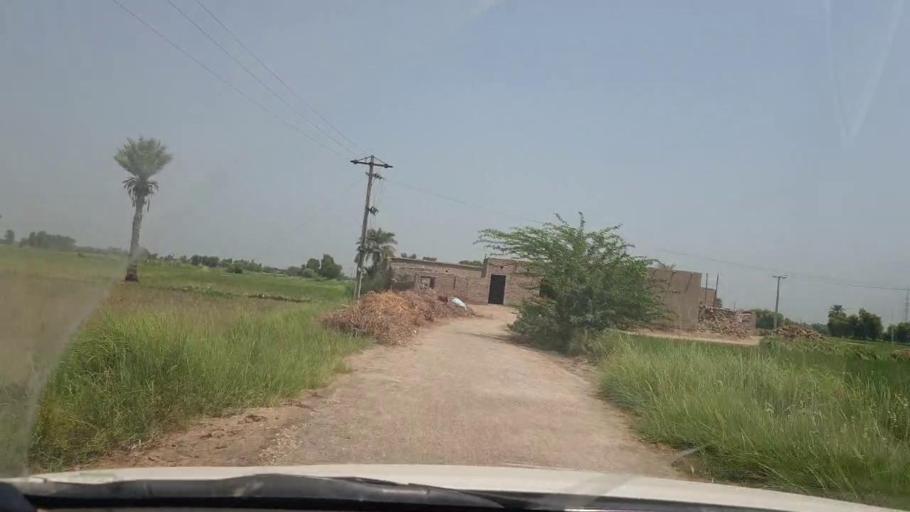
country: PK
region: Sindh
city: Shikarpur
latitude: 27.9338
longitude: 68.6688
